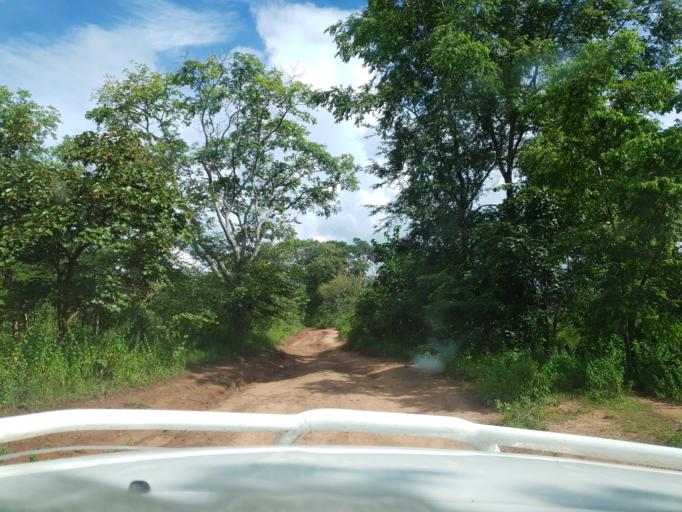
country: CI
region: Savanes
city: Tengrela
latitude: 10.4637
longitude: -6.7974
